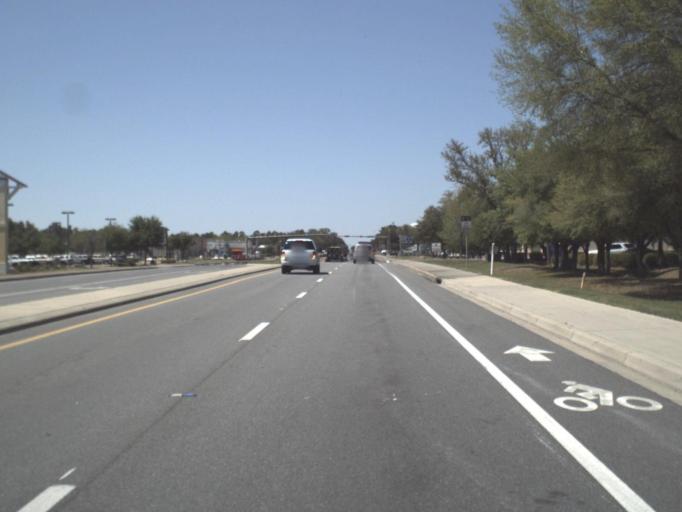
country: US
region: Florida
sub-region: Okaloosa County
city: Niceville
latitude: 30.4803
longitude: -86.4118
